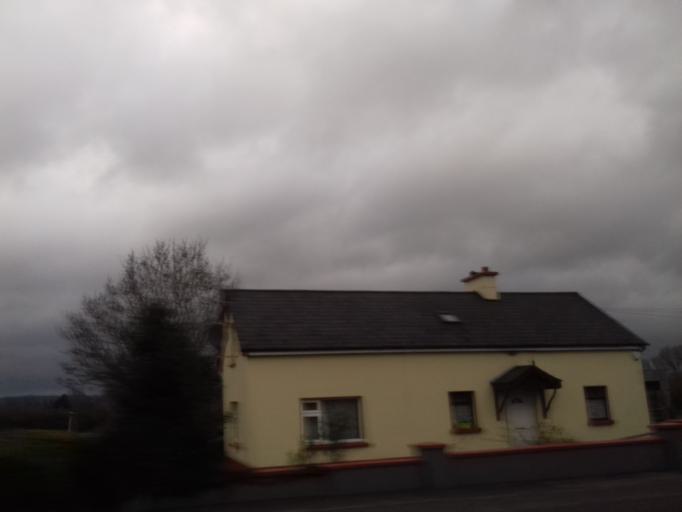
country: IE
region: Munster
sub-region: County Limerick
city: Newcastle West
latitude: 52.4613
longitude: -9.0303
